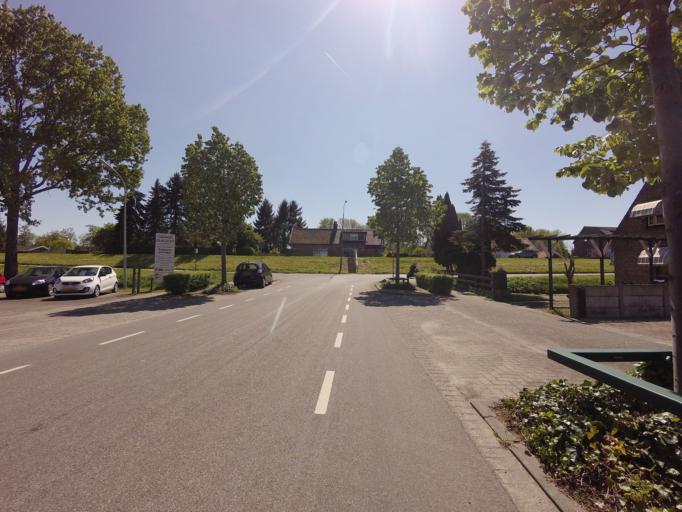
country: NL
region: South Holland
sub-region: Gemeente Dordrecht
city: Dordrecht
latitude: 51.7844
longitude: 4.6923
